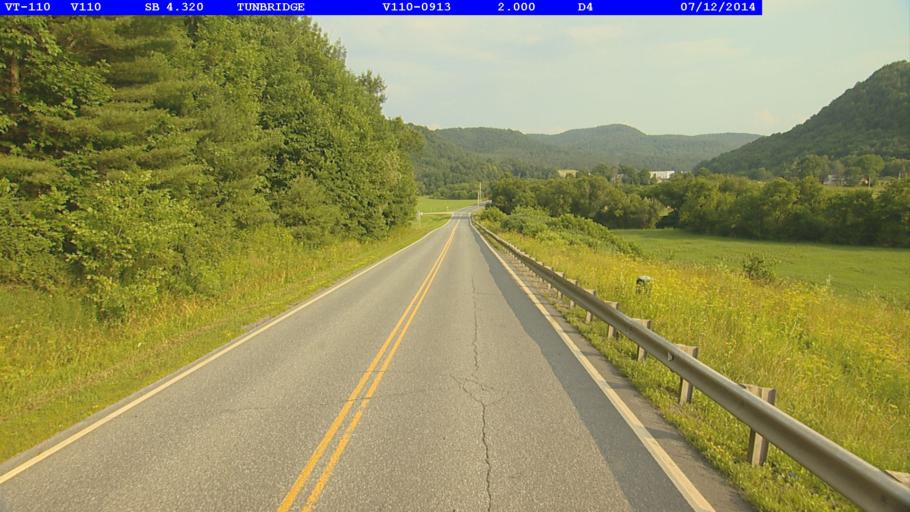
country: US
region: Vermont
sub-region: Orange County
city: Chelsea
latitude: 43.8792
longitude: -72.5013
